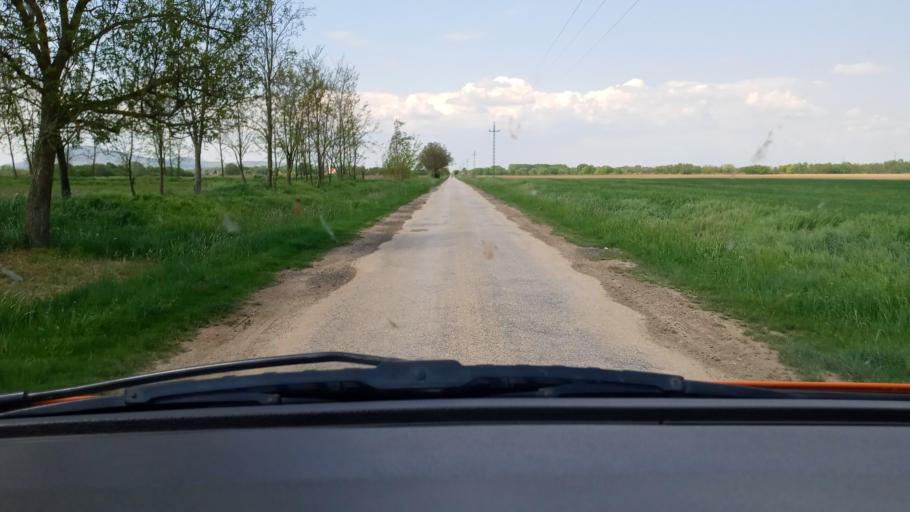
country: HU
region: Baranya
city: Beremend
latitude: 45.8087
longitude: 18.5162
